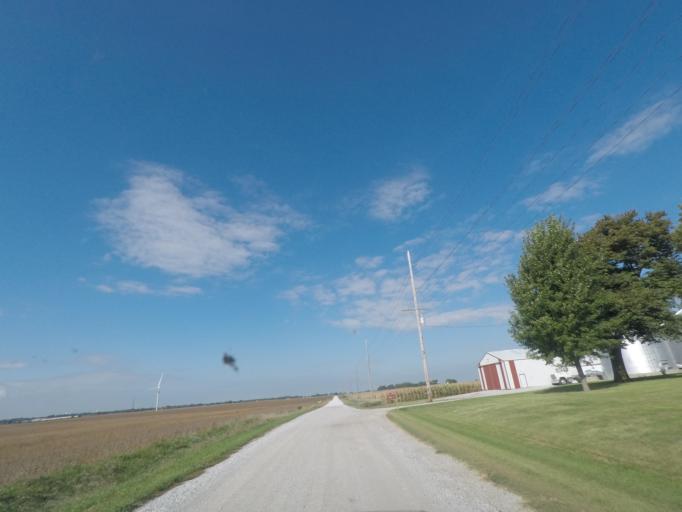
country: US
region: Iowa
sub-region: Story County
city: Nevada
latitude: 42.0344
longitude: -93.4124
